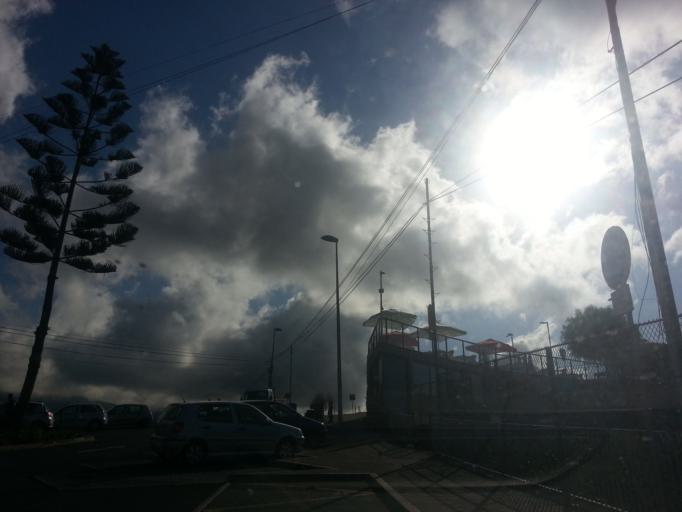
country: PT
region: Madeira
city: Camara de Lobos
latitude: 32.6592
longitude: -16.9408
